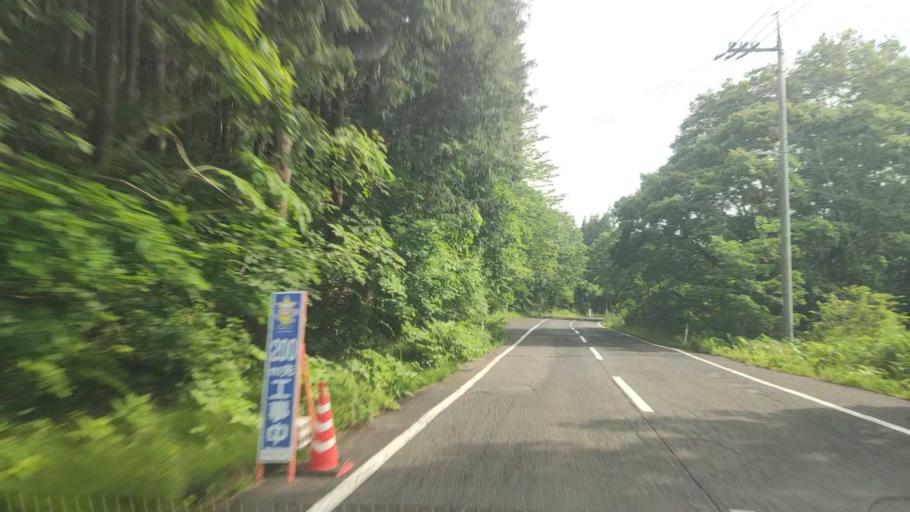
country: JP
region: Tottori
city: Kurayoshi
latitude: 35.3088
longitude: 134.0006
